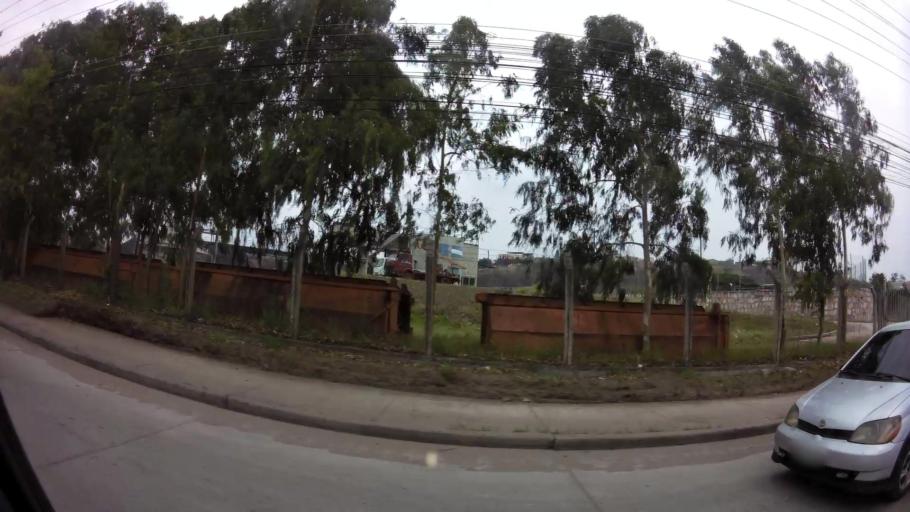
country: HN
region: Francisco Morazan
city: Tegucigalpa
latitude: 14.0672
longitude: -87.1994
